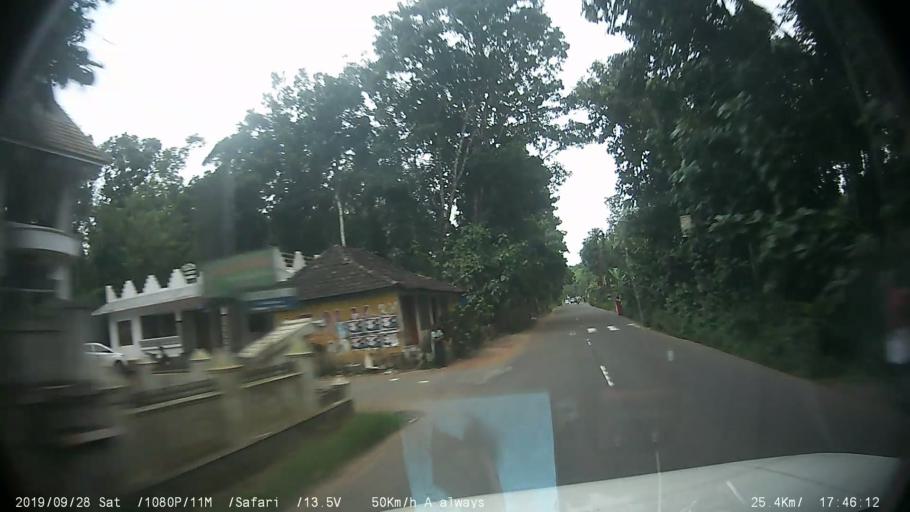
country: IN
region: Kerala
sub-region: Kottayam
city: Palackattumala
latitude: 9.7555
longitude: 76.5379
